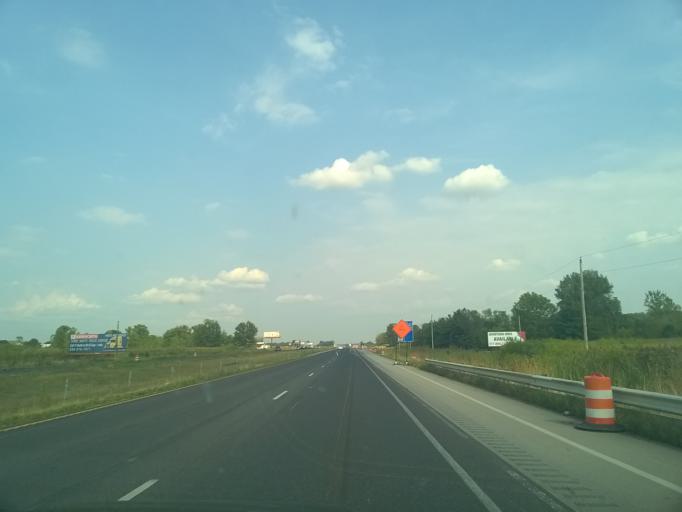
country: US
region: Indiana
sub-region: Vigo County
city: Terre Haute
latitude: 39.4306
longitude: -87.3474
